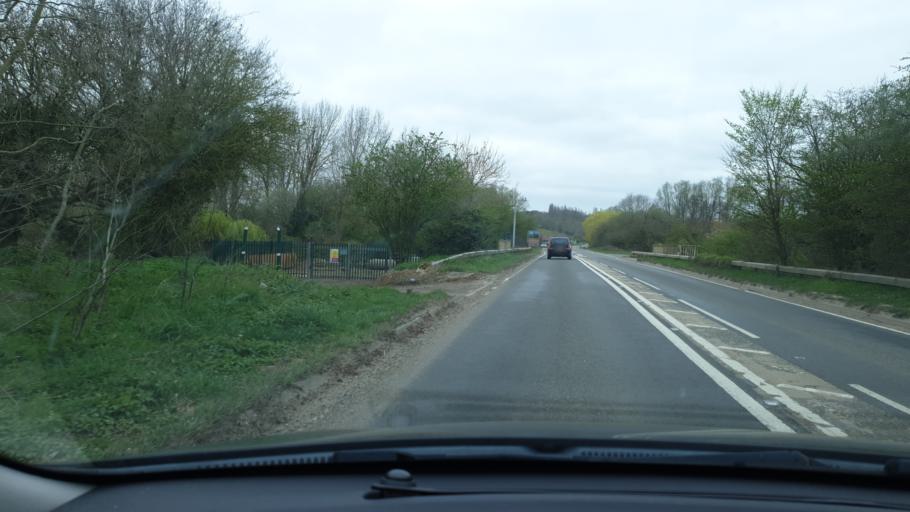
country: GB
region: England
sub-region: Essex
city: Great Horkesley
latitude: 51.9684
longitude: 0.8668
